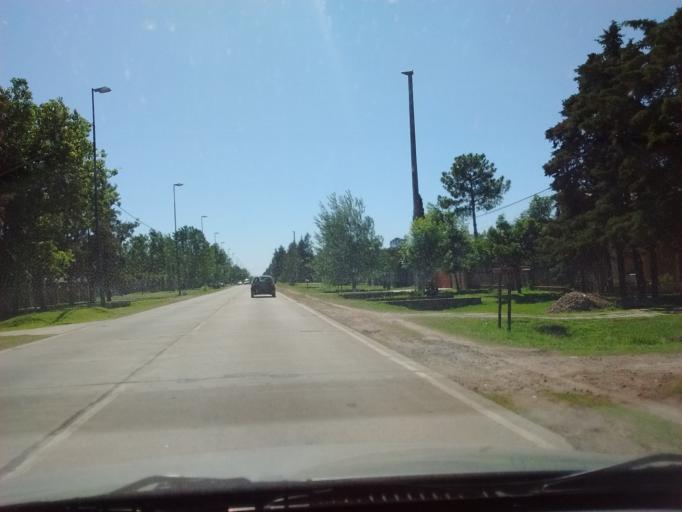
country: AR
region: Santa Fe
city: Funes
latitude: -32.9095
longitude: -60.7703
